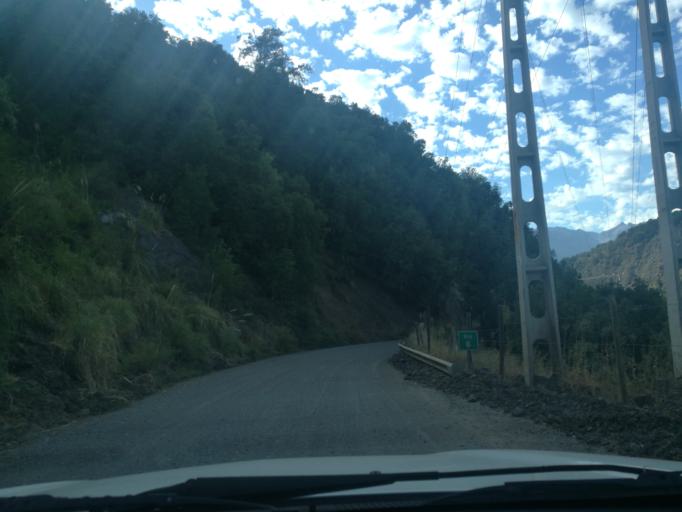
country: CL
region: O'Higgins
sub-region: Provincia de Cachapoal
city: Machali
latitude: -34.2772
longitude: -70.4481
